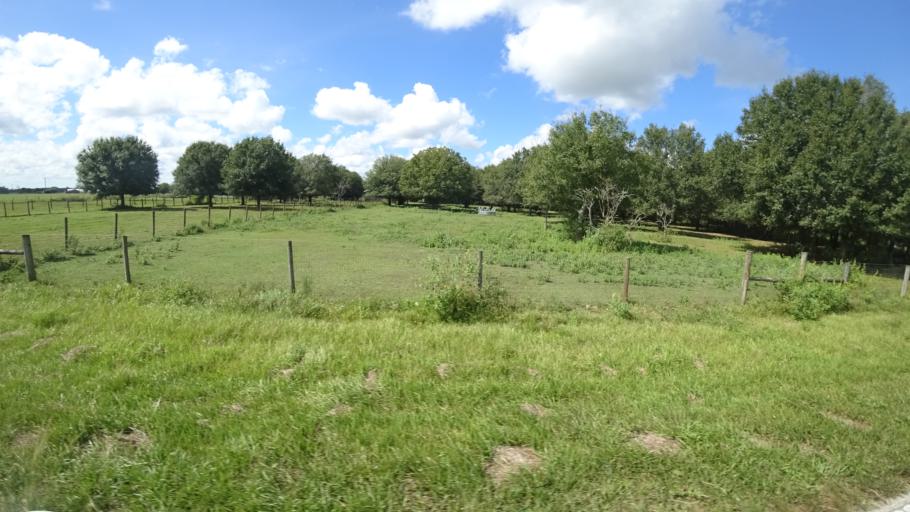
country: US
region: Florida
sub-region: Sarasota County
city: Lake Sarasota
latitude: 27.3694
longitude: -82.2194
